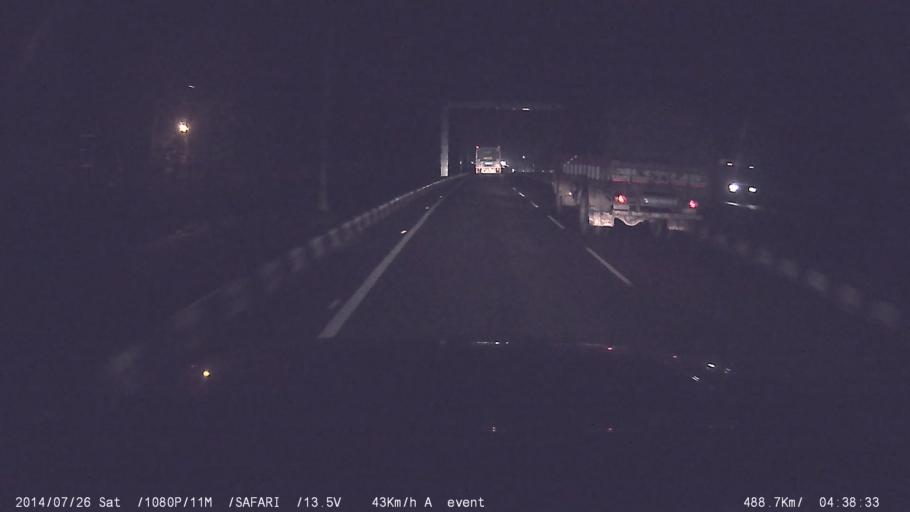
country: IN
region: Kerala
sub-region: Ernakulam
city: Angamali
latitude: 10.2429
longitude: 76.3729
